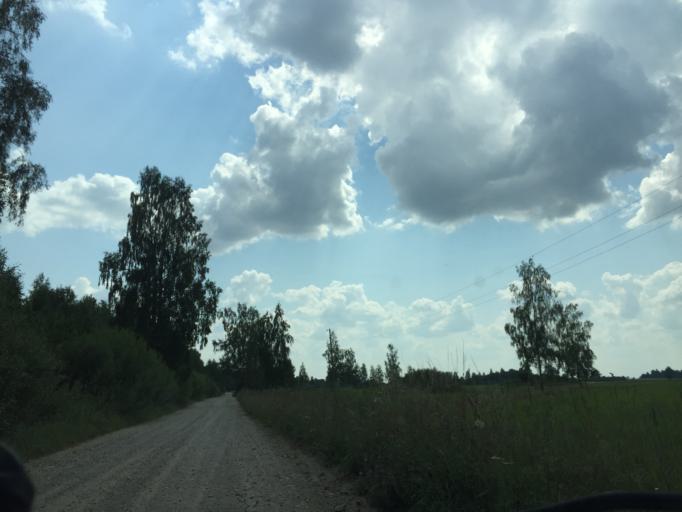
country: LT
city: Zagare
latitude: 56.3587
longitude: 23.1605
